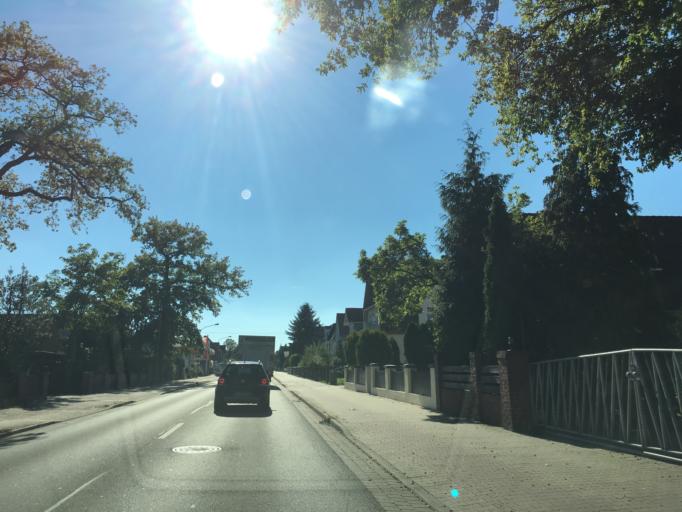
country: DE
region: Lower Saxony
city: Winsen
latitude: 53.3493
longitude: 10.2073
